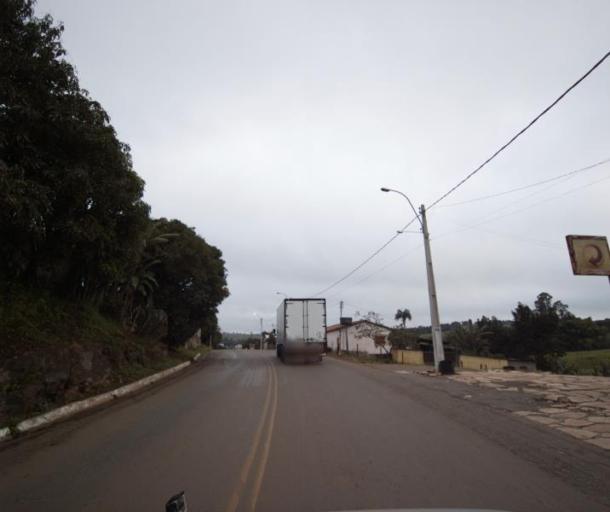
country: BR
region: Goias
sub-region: Pirenopolis
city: Pirenopolis
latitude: -15.9306
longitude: -48.8049
